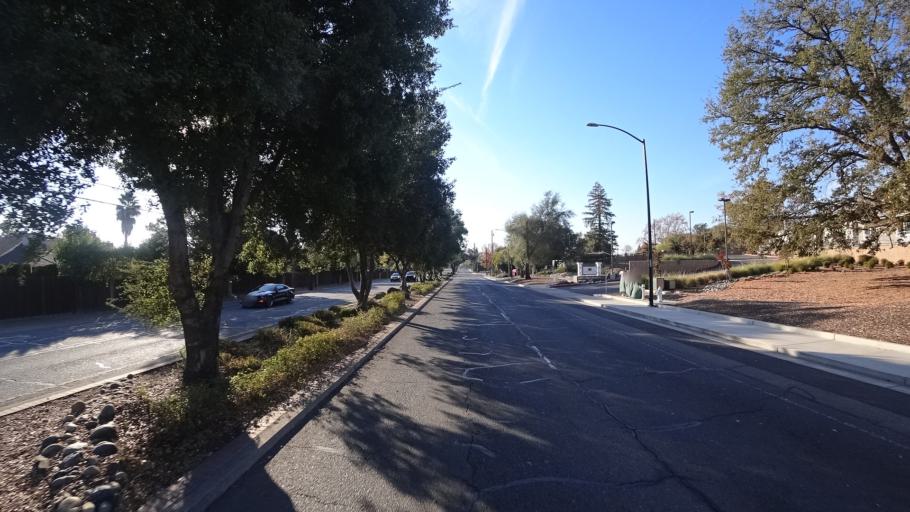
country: US
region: California
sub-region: Sacramento County
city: Citrus Heights
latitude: 38.6911
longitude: -121.2717
